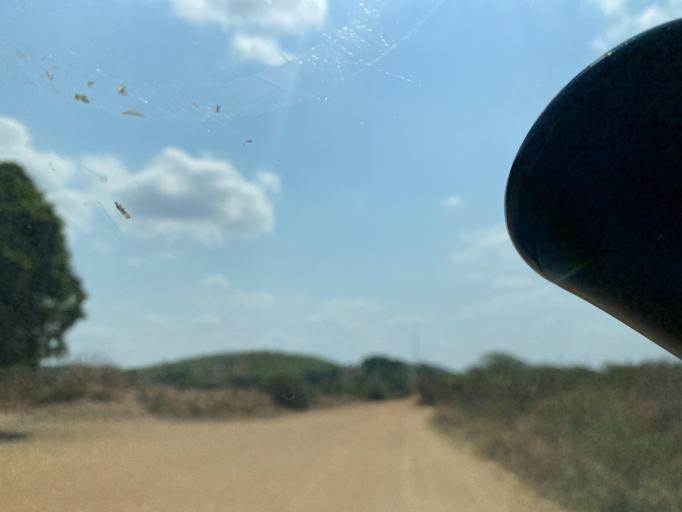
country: ZM
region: Lusaka
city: Chongwe
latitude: -15.6034
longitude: 28.7429
